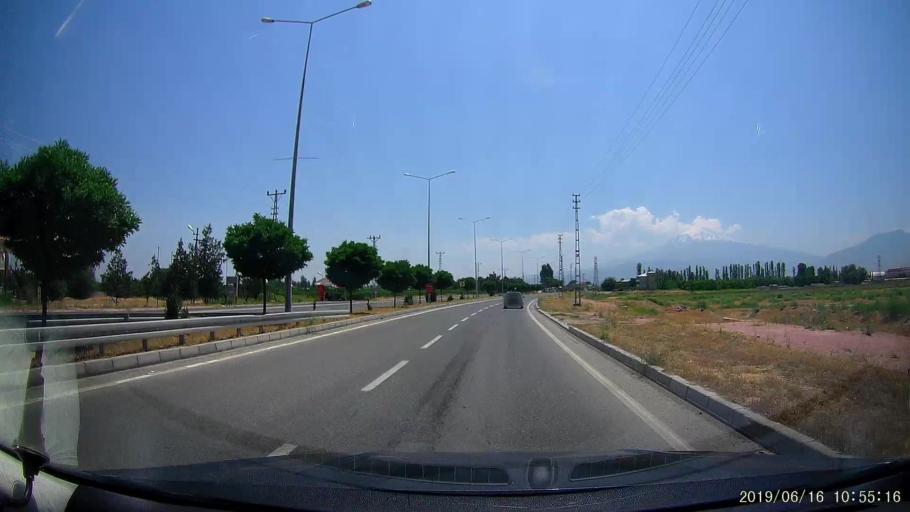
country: TR
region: Igdir
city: Igdir
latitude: 39.9370
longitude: 44.0085
